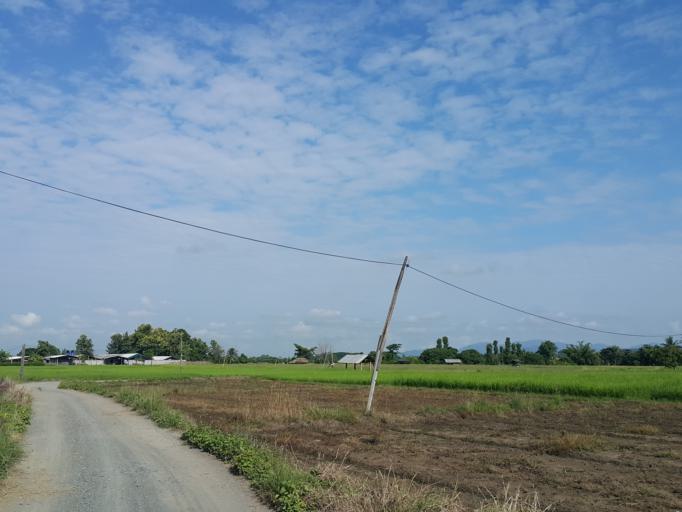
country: TH
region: Chiang Mai
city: San Kamphaeng
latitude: 18.8239
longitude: 99.1647
